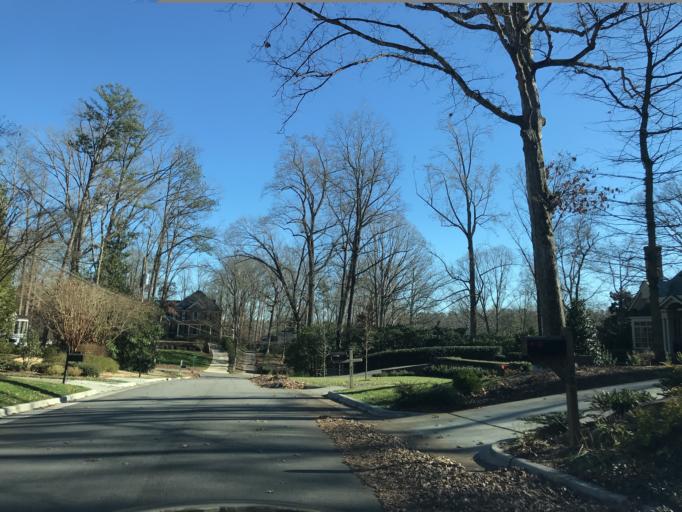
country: US
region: North Carolina
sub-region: Wake County
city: West Raleigh
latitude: 35.8261
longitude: -78.6542
